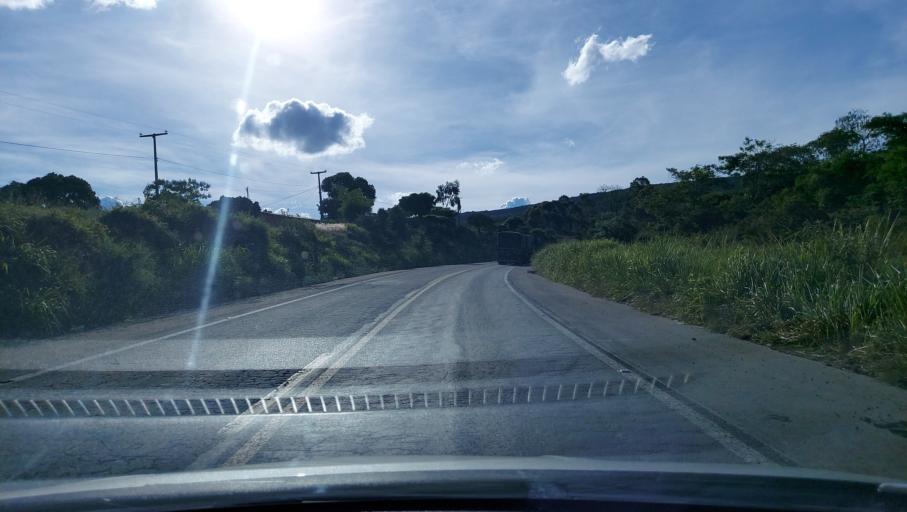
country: BR
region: Bahia
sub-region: Seabra
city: Seabra
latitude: -12.4092
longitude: -41.8669
